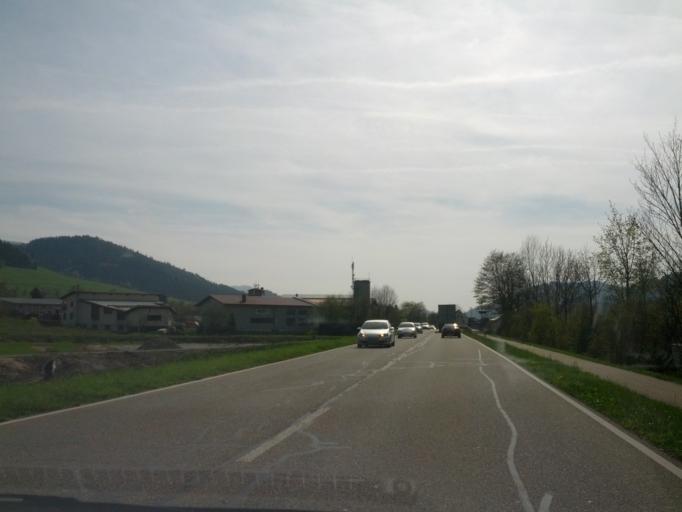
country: DE
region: Baden-Wuerttemberg
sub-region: Freiburg Region
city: Elzach
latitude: 48.1486
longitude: 8.0299
